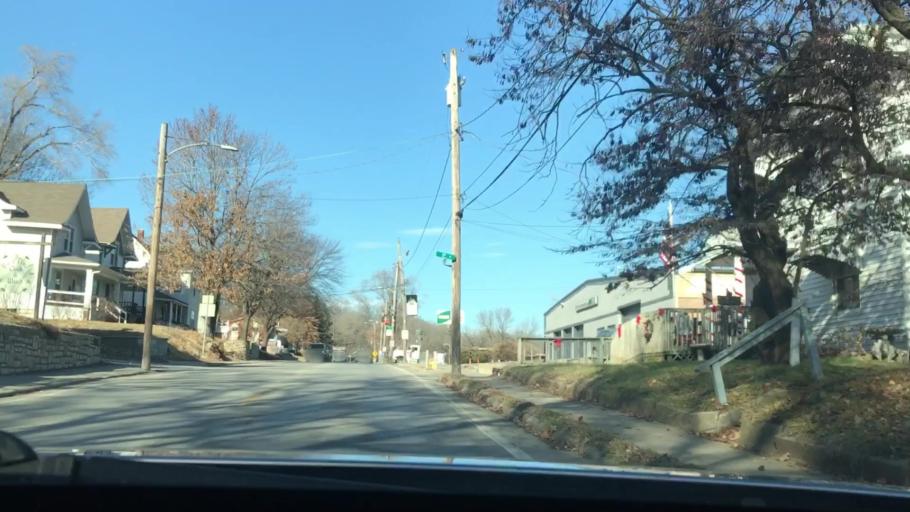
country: US
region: Missouri
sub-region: Platte County
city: Parkville
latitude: 39.1901
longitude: -94.6829
